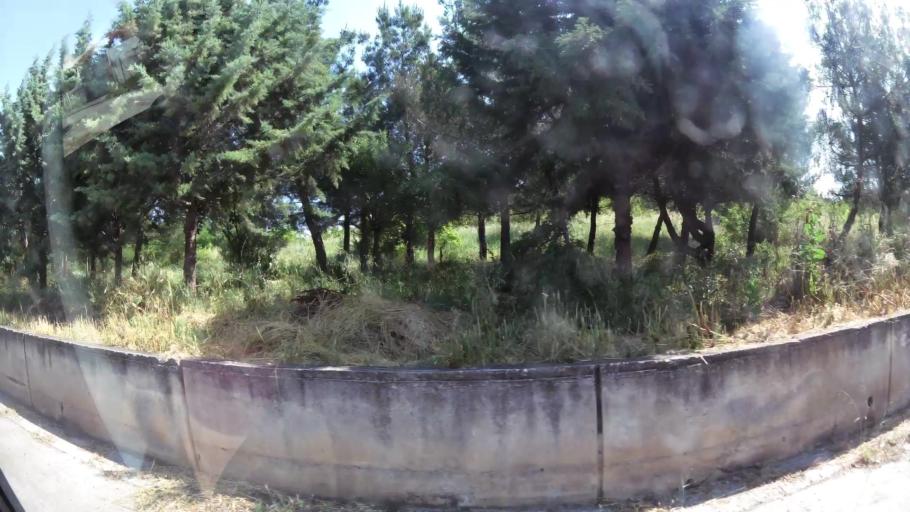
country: GR
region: West Macedonia
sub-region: Nomos Kozanis
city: Koila
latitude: 40.3380
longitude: 21.7884
